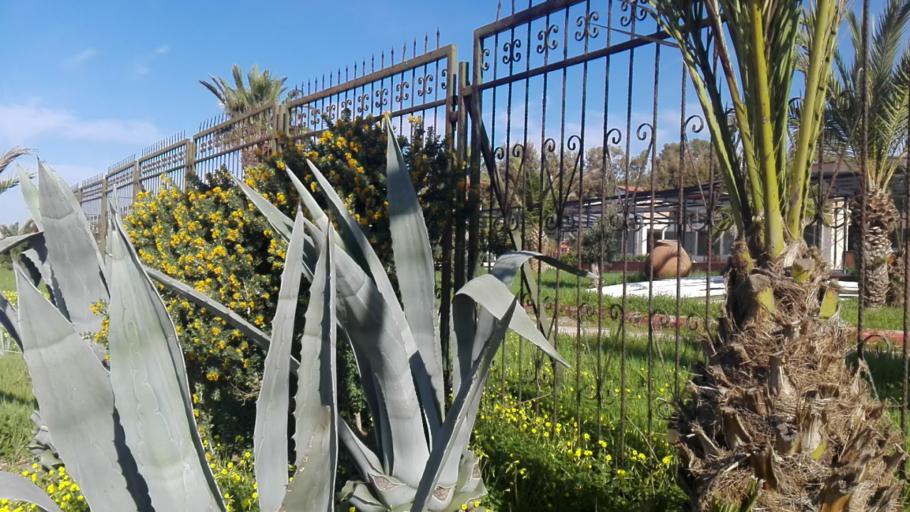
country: TR
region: Antalya
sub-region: Alanya
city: Payallar
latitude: 36.5786
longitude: 31.8833
